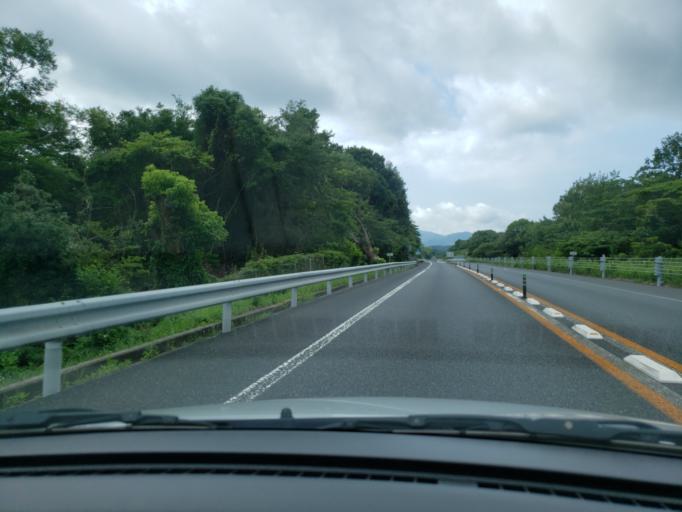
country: JP
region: Hiroshima
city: Innoshima
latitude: 34.2418
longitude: 133.0478
